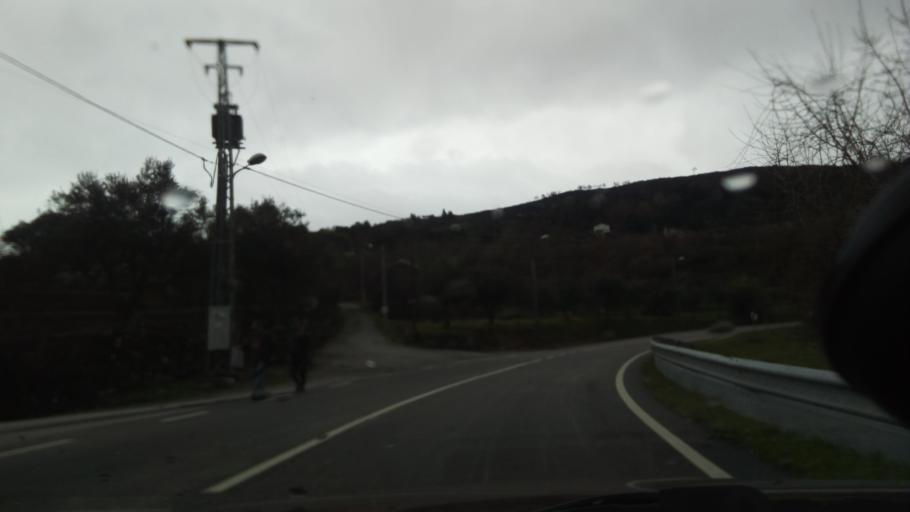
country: PT
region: Guarda
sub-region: Manteigas
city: Manteigas
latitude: 40.5043
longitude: -7.5842
